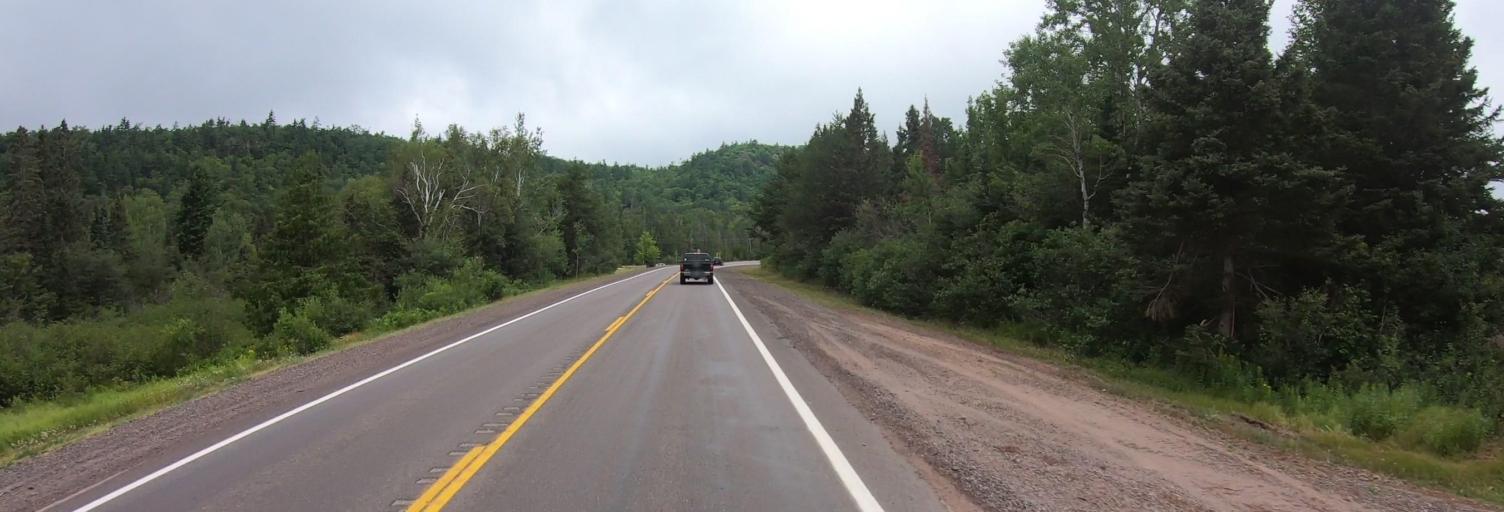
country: US
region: Michigan
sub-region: Keweenaw County
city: Eagle River
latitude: 47.3748
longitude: -88.3042
